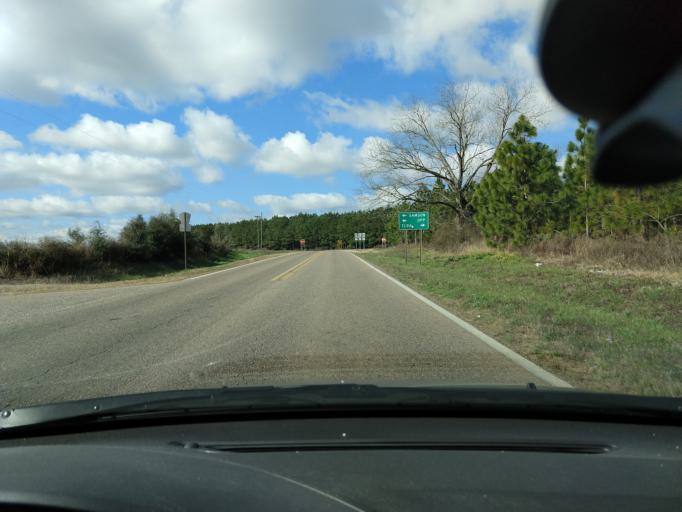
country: US
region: Alabama
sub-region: Coffee County
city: Elba
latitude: 31.3113
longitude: -86.0317
